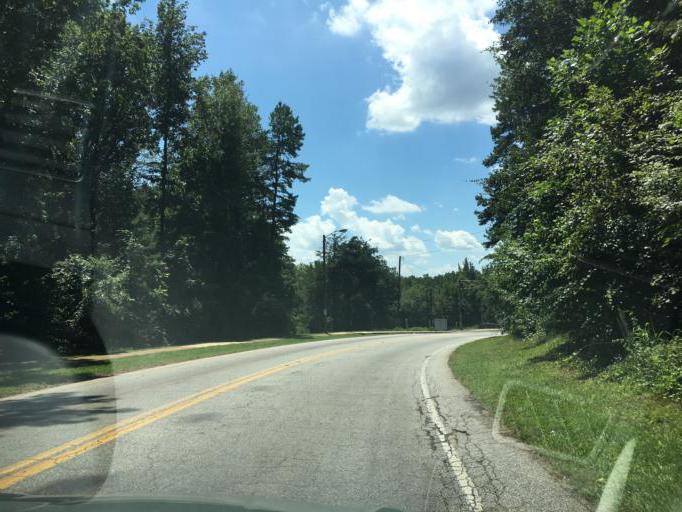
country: US
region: South Carolina
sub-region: Spartanburg County
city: Lyman
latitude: 34.9426
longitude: -82.1218
